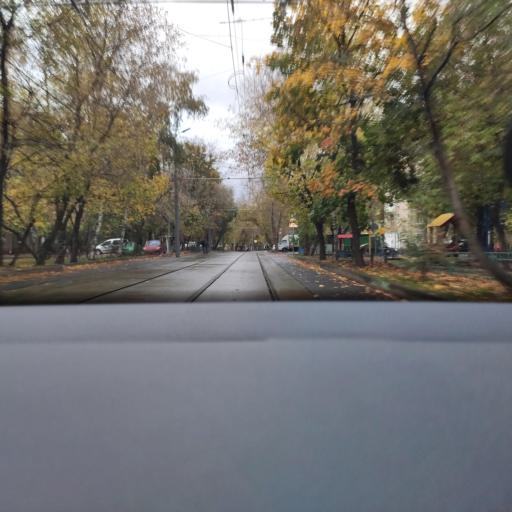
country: RU
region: Moskovskaya
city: Koptevo
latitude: 55.8288
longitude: 37.5189
